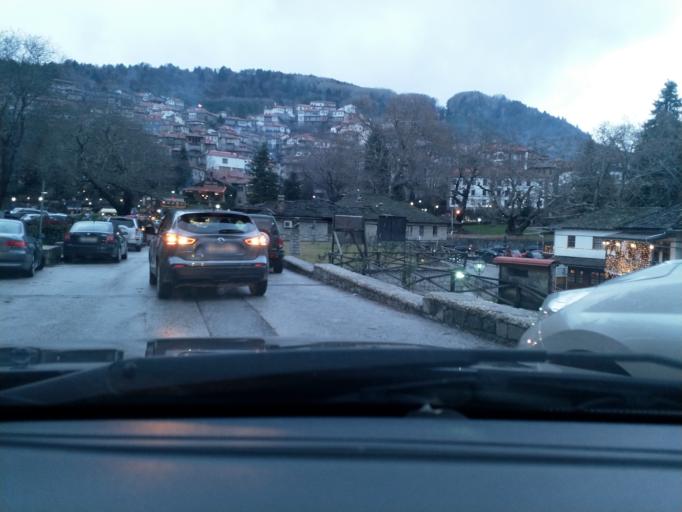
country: GR
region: Epirus
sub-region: Nomos Ioanninon
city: Metsovo
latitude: 39.7696
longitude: 21.1841
